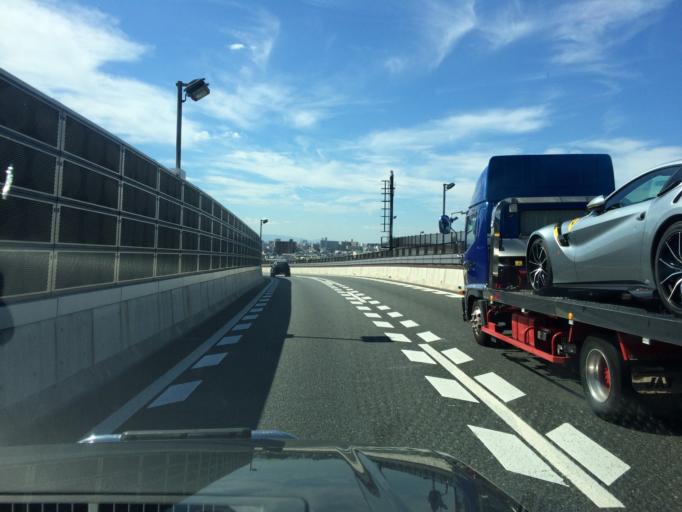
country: JP
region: Osaka
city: Kadoma
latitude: 34.7157
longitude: 135.5911
